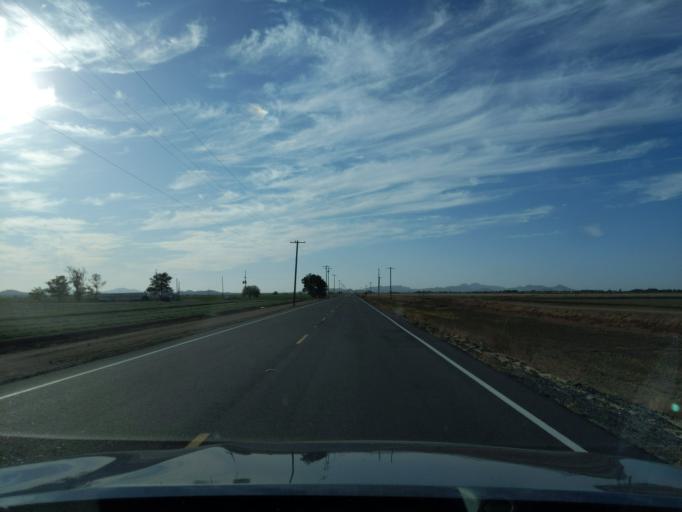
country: US
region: Arizona
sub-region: Pinal County
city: Florence
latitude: 33.1184
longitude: -111.4203
